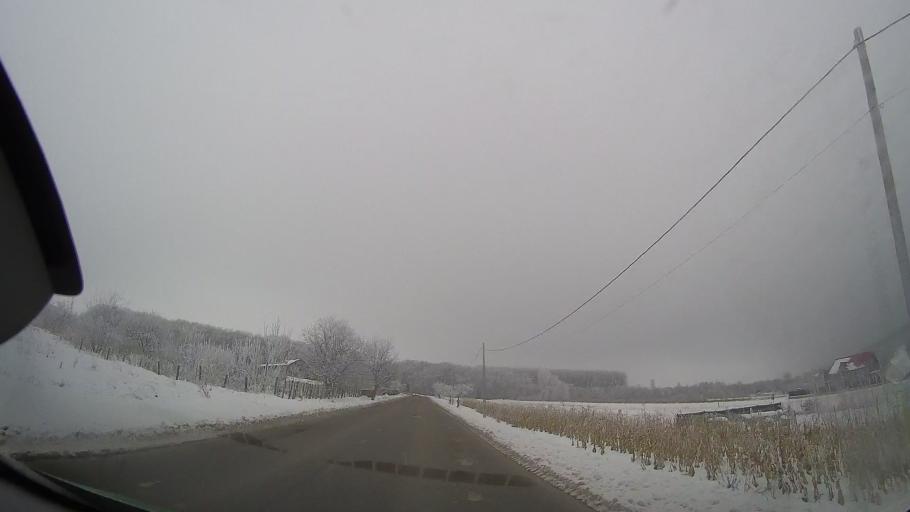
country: RO
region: Neamt
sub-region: Comuna Horia
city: Cotu Vames
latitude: 46.8786
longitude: 26.9747
